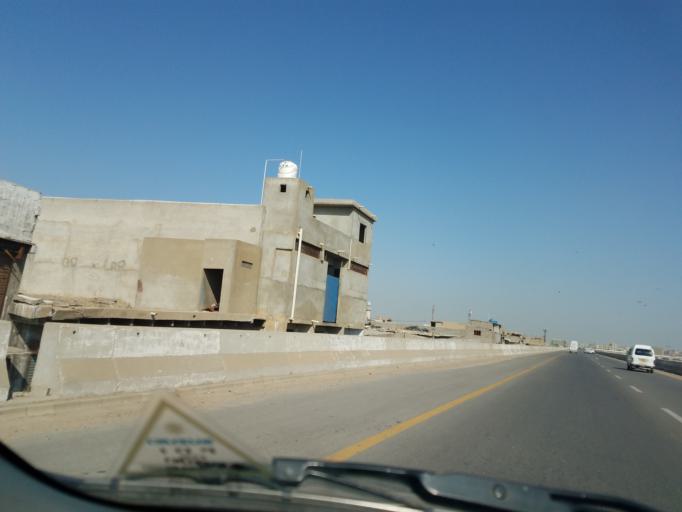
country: PK
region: Sindh
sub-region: Karachi District
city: Karachi
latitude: 24.8821
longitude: 66.9976
